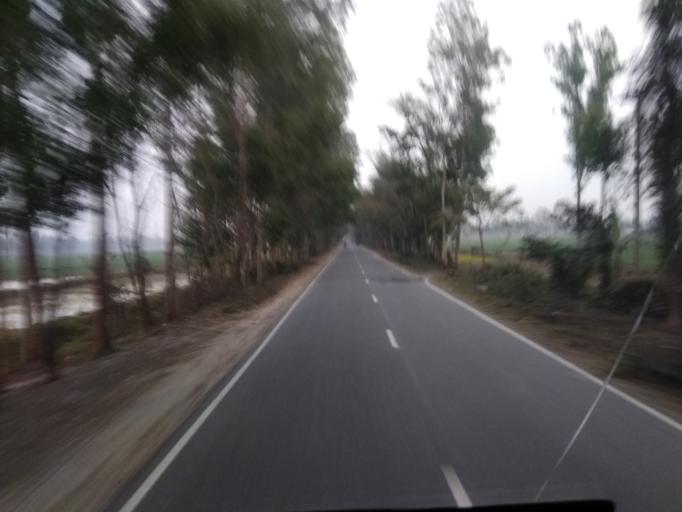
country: BD
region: Rajshahi
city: Bogra
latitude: 24.6721
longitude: 89.2791
